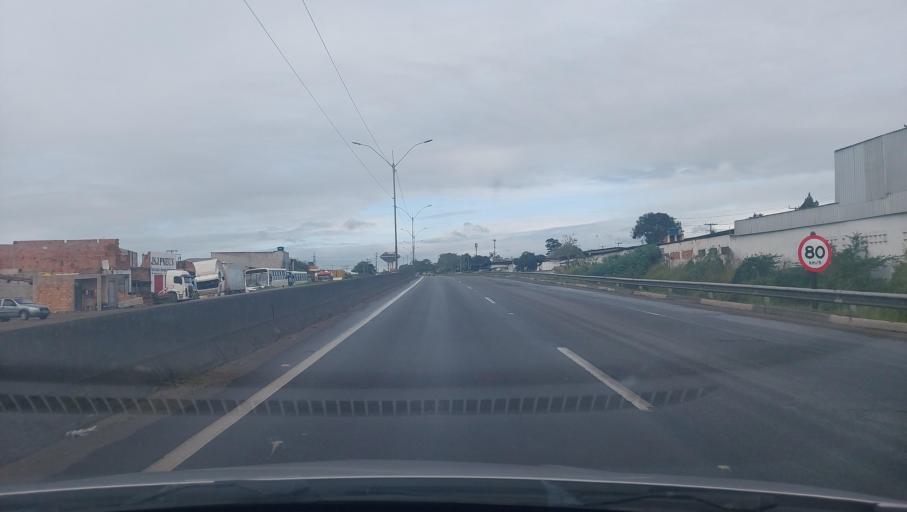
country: BR
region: Bahia
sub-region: Feira De Santana
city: Feira de Santana
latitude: -12.2860
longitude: -38.9680
